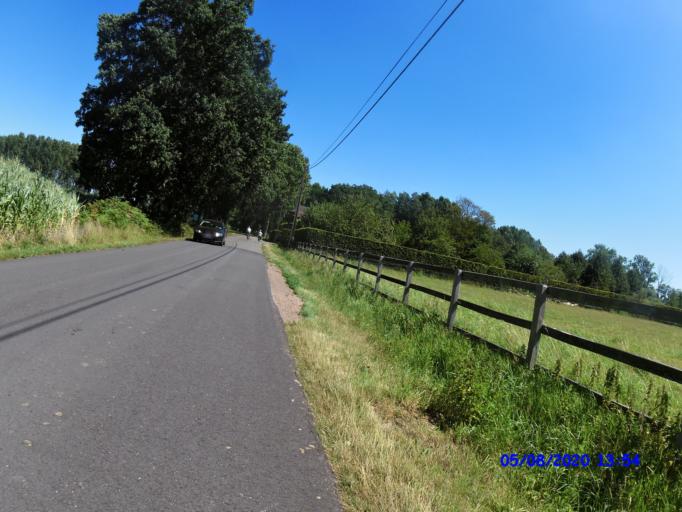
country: BE
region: Flanders
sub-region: Provincie Antwerpen
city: Hoogstraten
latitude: 51.3876
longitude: 4.7873
